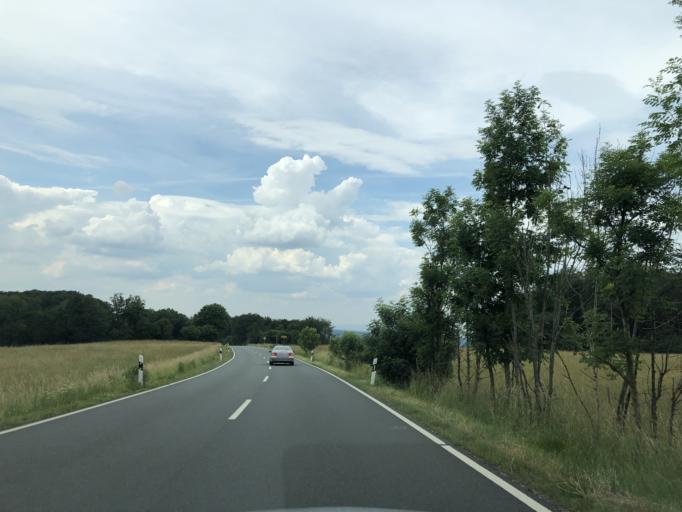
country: DE
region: Hesse
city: Lutzelbach
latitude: 49.7353
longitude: 8.7694
